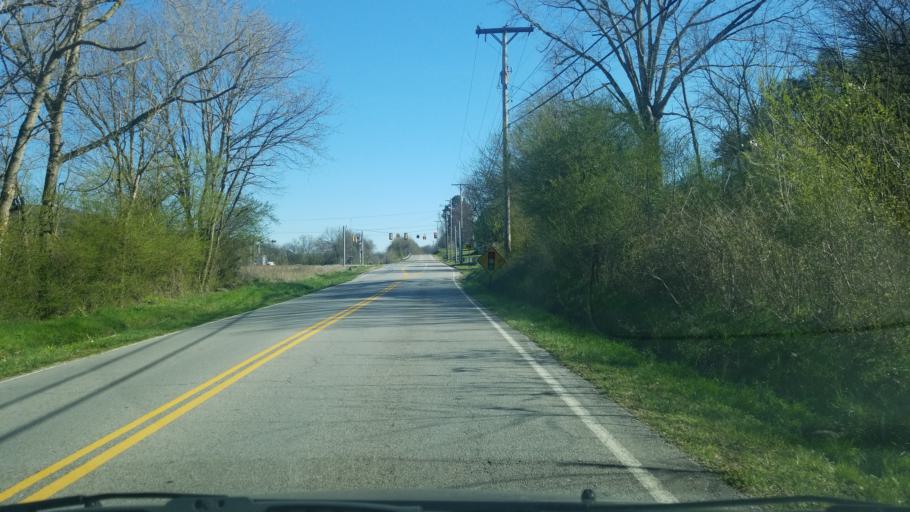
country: US
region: Tennessee
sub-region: Hamilton County
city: Soddy-Daisy
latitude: 35.2304
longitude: -85.1944
